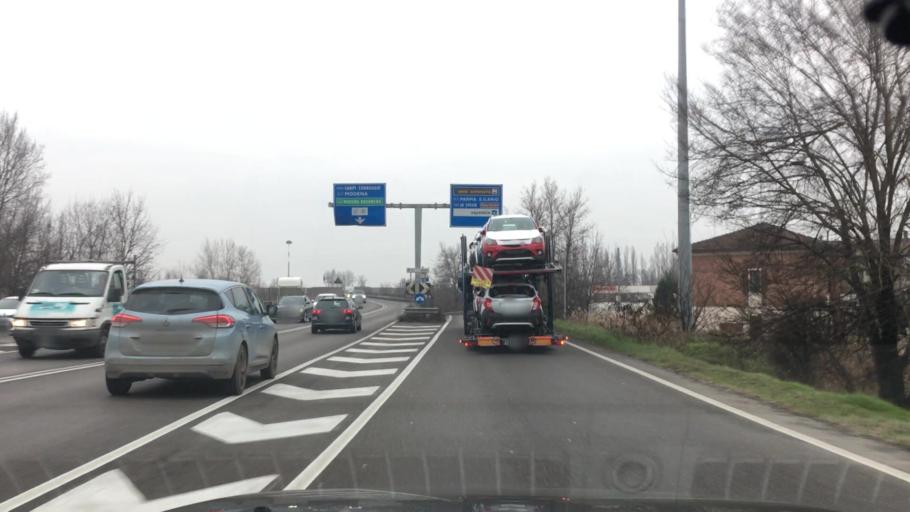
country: IT
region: Emilia-Romagna
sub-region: Provincia di Reggio Emilia
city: Reggio nell'Emilia
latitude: 44.7207
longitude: 10.6239
